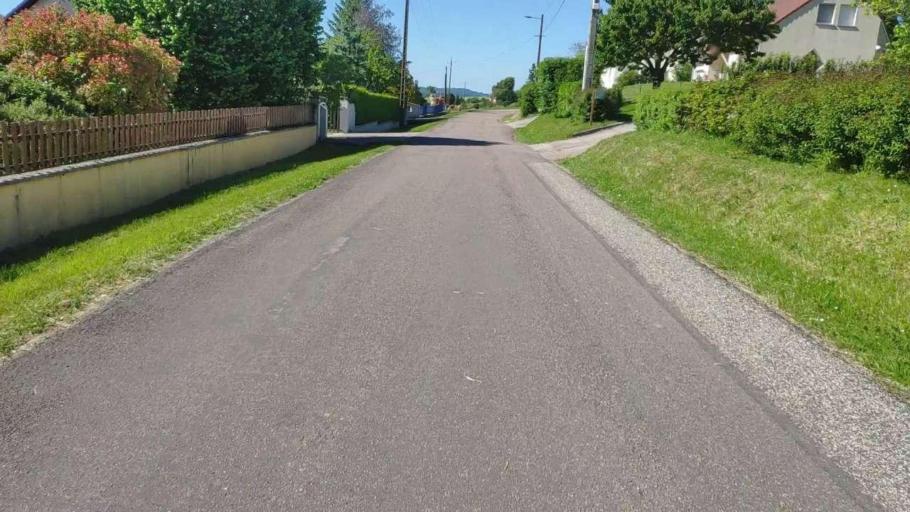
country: FR
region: Franche-Comte
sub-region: Departement du Jura
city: Perrigny
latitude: 46.7179
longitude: 5.5764
